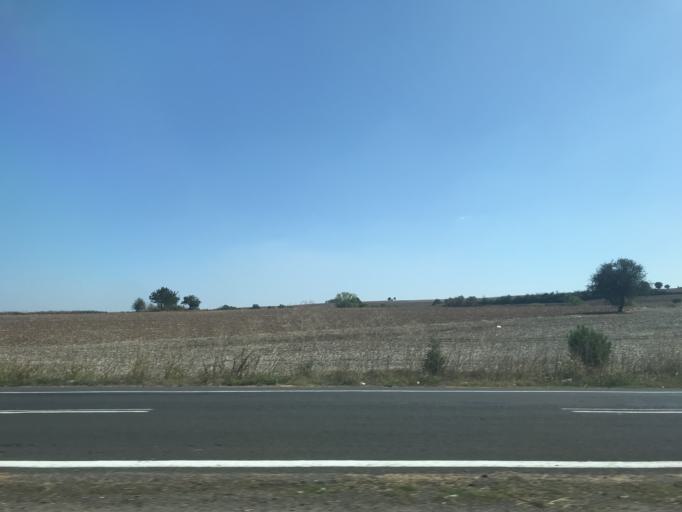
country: TR
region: Tekirdag
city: Muratli
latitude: 41.1386
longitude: 27.4922
